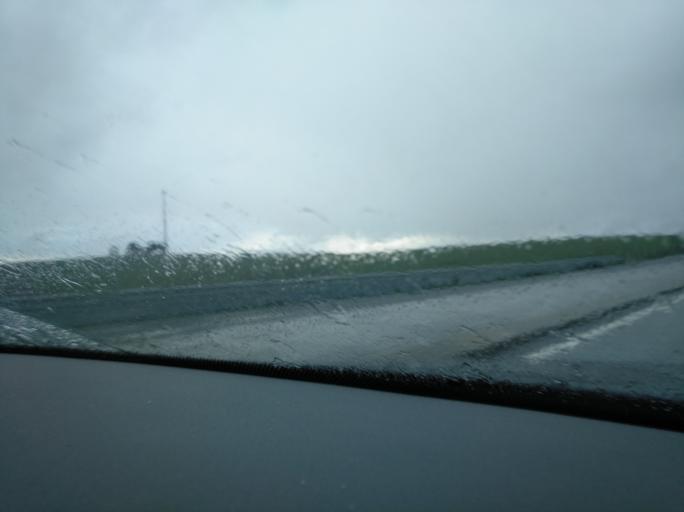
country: PT
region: Beja
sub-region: Castro Verde
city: Castro Verde
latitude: 37.7055
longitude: -7.9346
